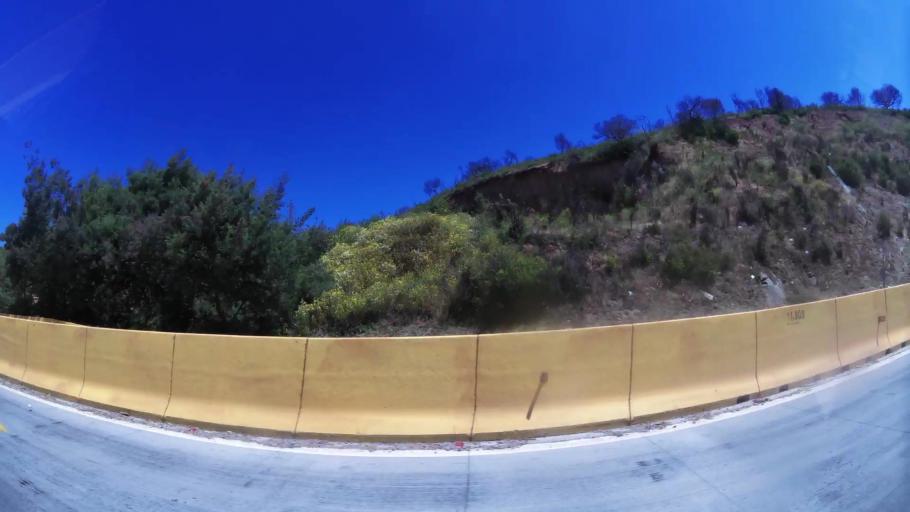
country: CL
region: Valparaiso
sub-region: Provincia de Valparaiso
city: Valparaiso
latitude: -33.0606
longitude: -71.6446
